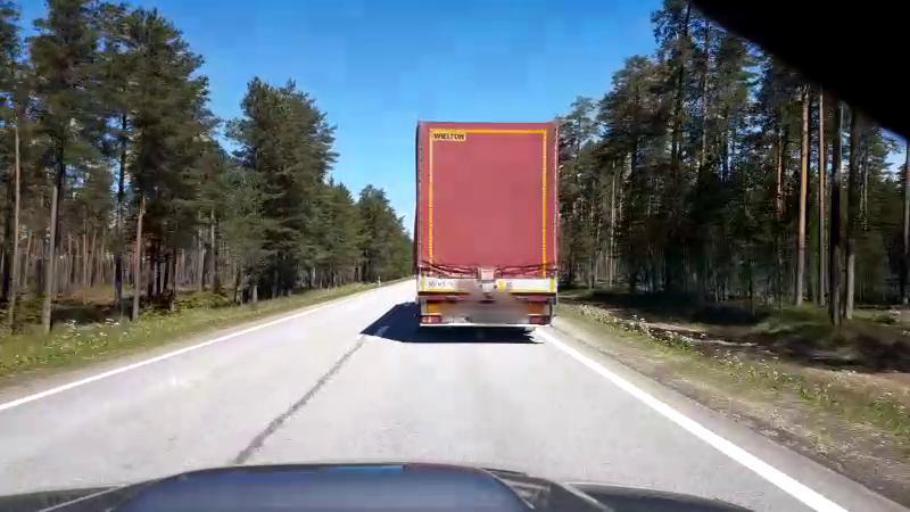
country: LV
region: Salacgrivas
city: Salacgriva
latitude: 57.5478
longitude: 24.4325
